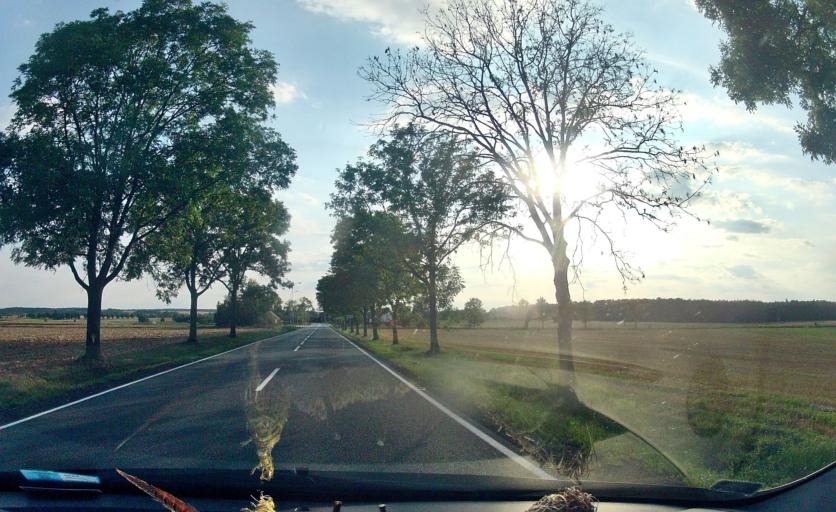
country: PL
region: Opole Voivodeship
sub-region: Powiat oleski
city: Gorzow Slaski
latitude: 51.0174
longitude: 18.3881
